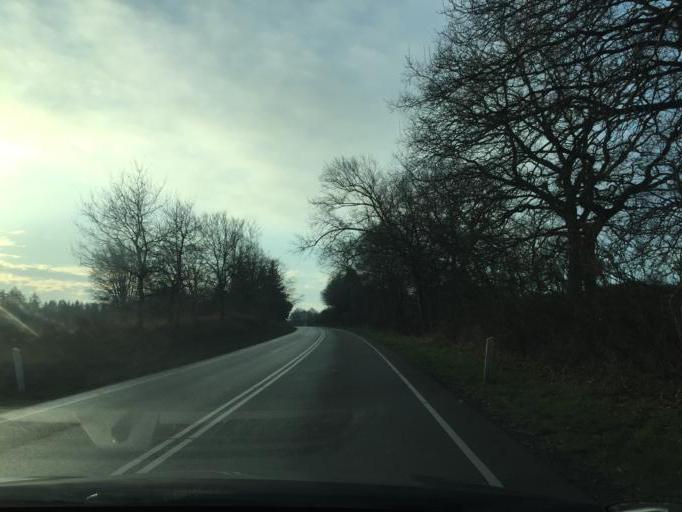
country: DK
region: South Denmark
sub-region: Faaborg-Midtfyn Kommune
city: Faaborg
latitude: 55.1558
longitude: 10.2692
